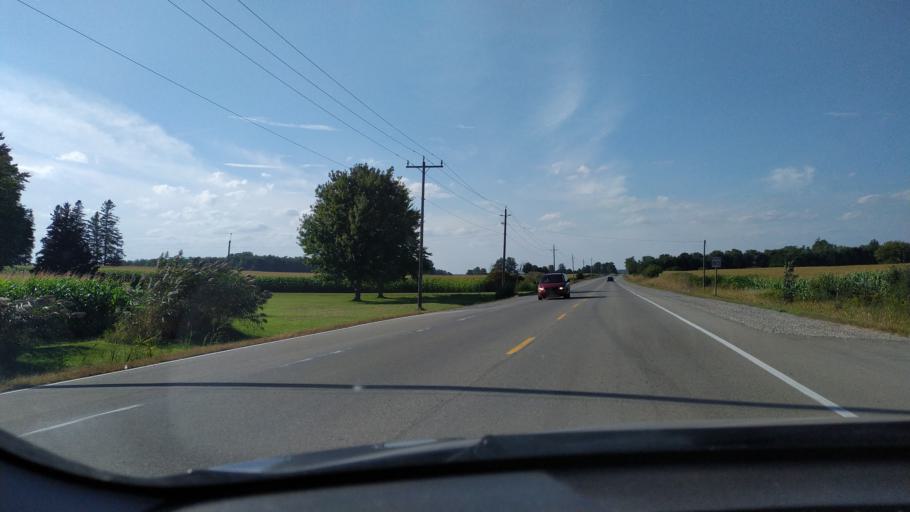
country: CA
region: Ontario
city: Ingersoll
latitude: 43.0550
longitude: -80.8274
